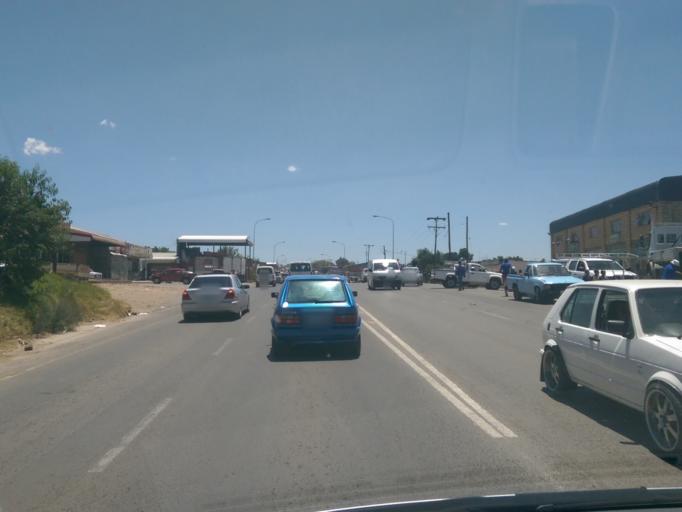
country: LS
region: Maseru
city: Maseru
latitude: -29.3426
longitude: 27.5149
